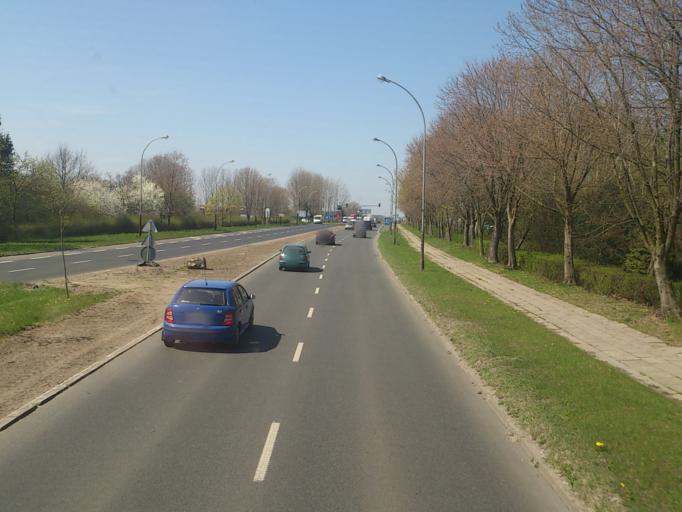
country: PL
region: Lodz Voivodeship
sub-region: Piotrkow Trybunalski
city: Piotrkow Trybunalski
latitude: 51.4072
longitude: 19.6508
